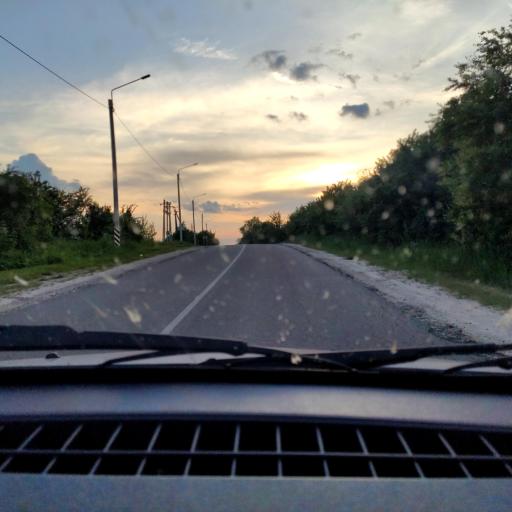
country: RU
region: Voronezj
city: Ramon'
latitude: 51.9514
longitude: 39.3672
